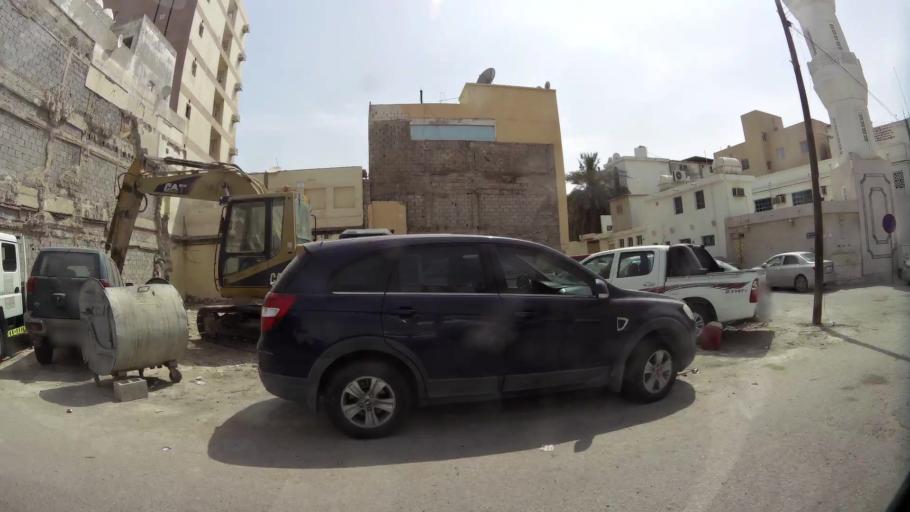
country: QA
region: Baladiyat ad Dawhah
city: Doha
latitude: 25.2804
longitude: 51.5407
